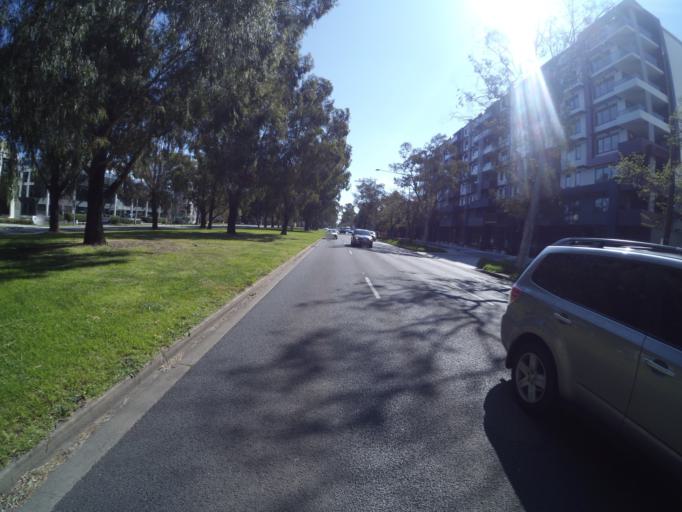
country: AU
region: Australian Capital Territory
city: Canberra
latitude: -35.2716
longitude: 149.1305
